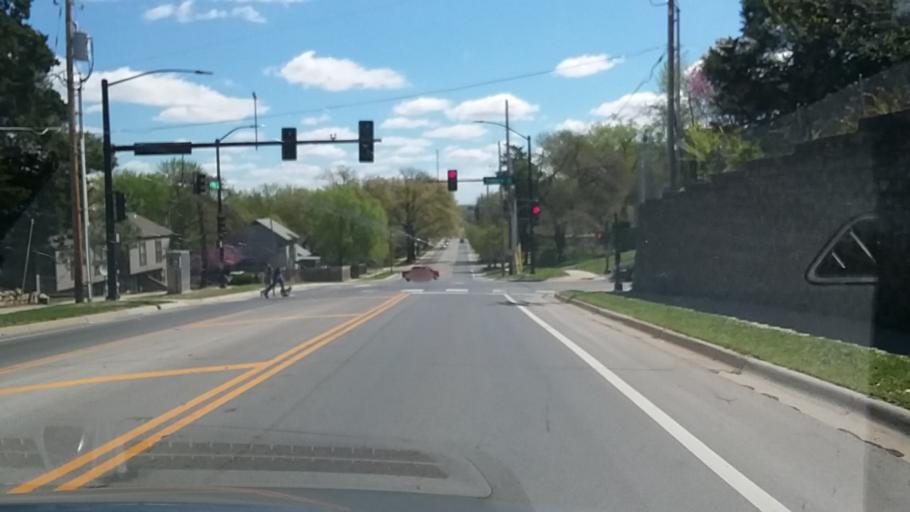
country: US
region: Kansas
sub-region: Douglas County
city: Lawrence
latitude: 38.9675
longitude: -95.2516
